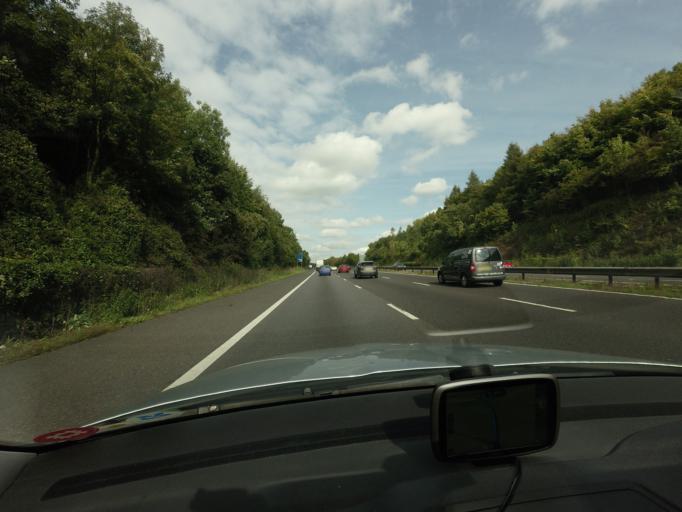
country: GB
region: England
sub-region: Kent
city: Shoreham
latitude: 51.3242
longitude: 0.1591
